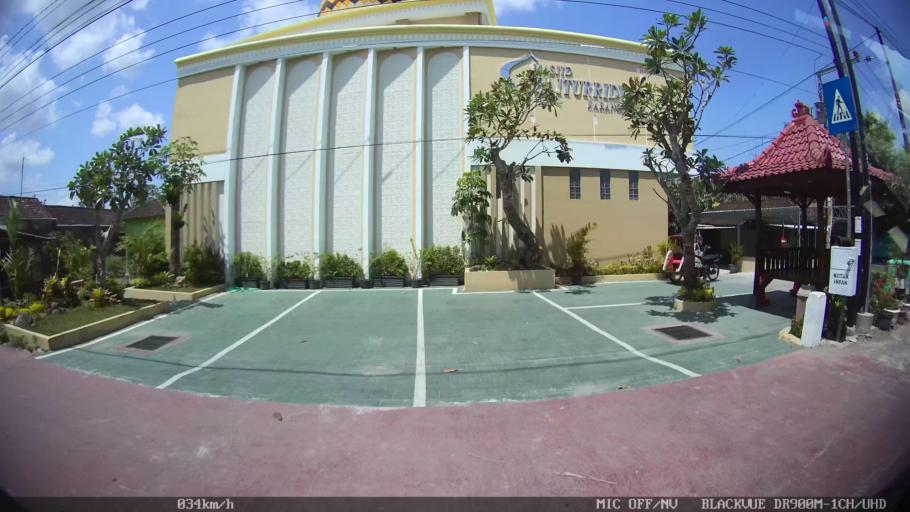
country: ID
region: Daerah Istimewa Yogyakarta
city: Sewon
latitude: -7.9014
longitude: 110.3839
